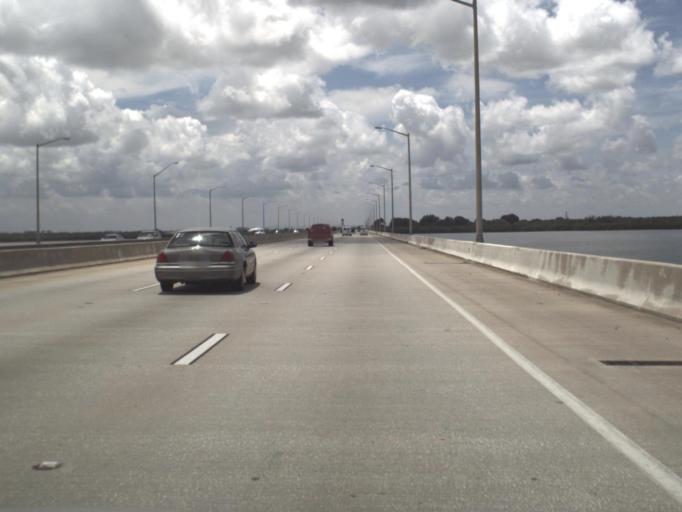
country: US
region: Florida
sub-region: Pinellas County
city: South Highpoint
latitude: 27.9378
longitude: -82.7029
